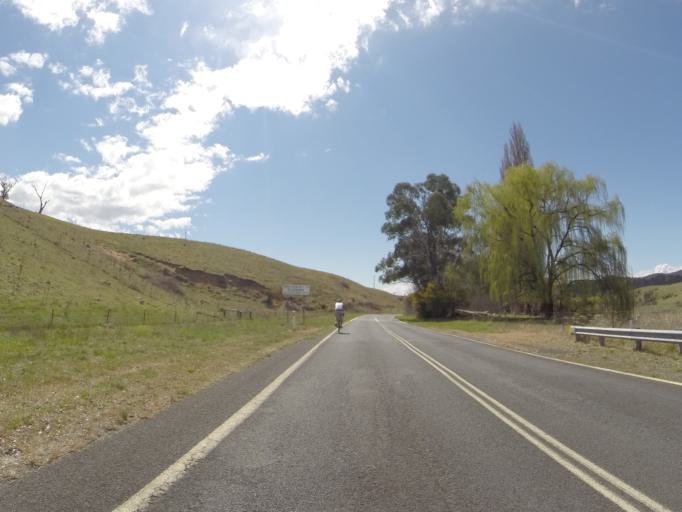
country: AU
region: Australian Capital Territory
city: Macarthur
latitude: -35.3998
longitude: 148.9601
